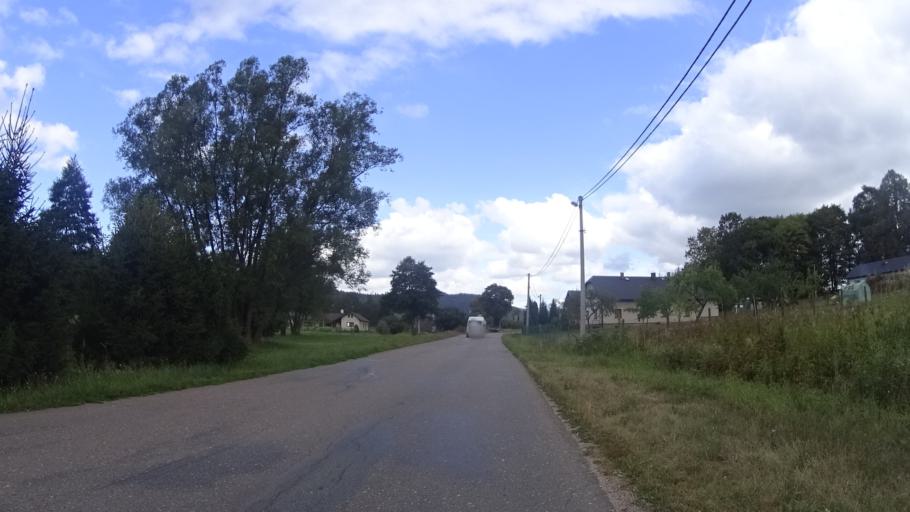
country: CZ
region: Pardubicky
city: Dolni Dobrouc
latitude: 49.9431
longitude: 16.5214
